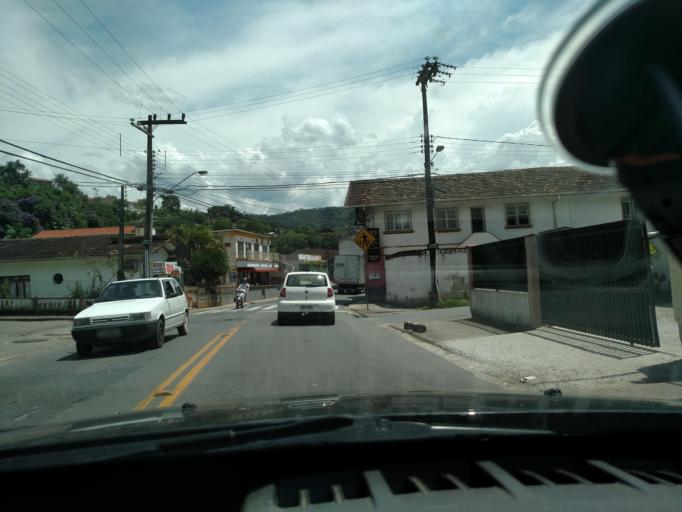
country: BR
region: Santa Catarina
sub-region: Blumenau
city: Blumenau
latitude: -26.9699
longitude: -49.0736
